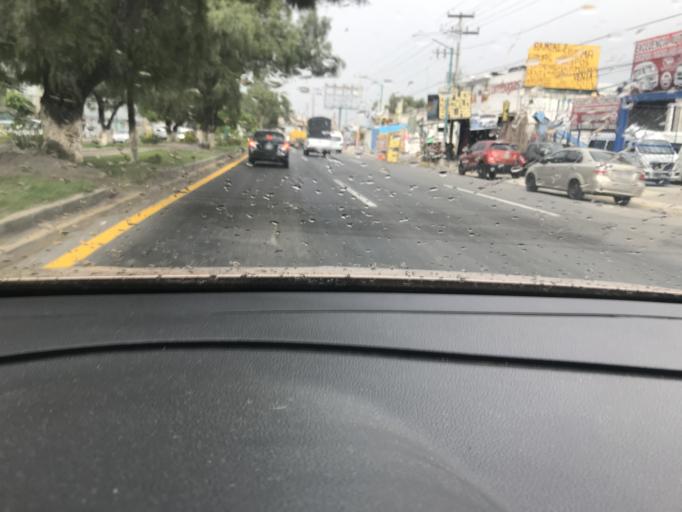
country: MX
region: Mexico
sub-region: La Paz
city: Arenal
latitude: 19.3884
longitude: -98.9365
